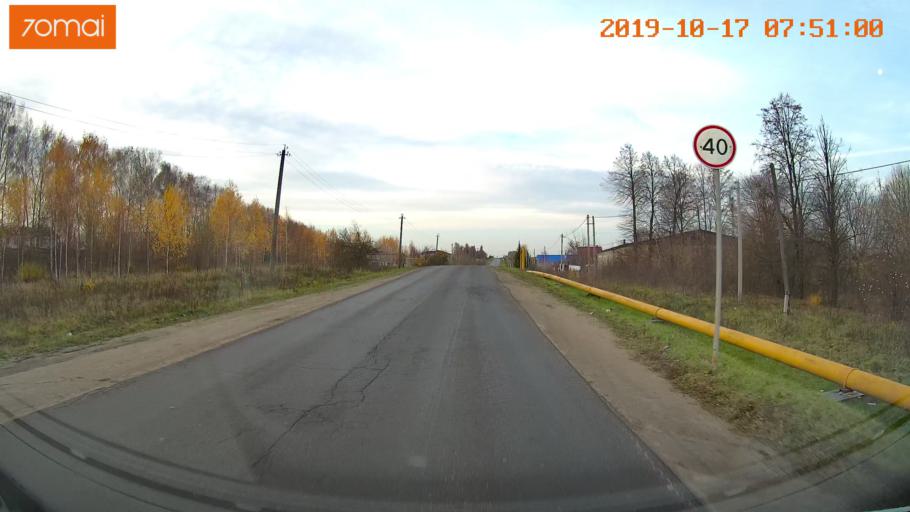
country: RU
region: Vladimir
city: Yur'yev-Pol'skiy
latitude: 56.4832
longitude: 39.6589
